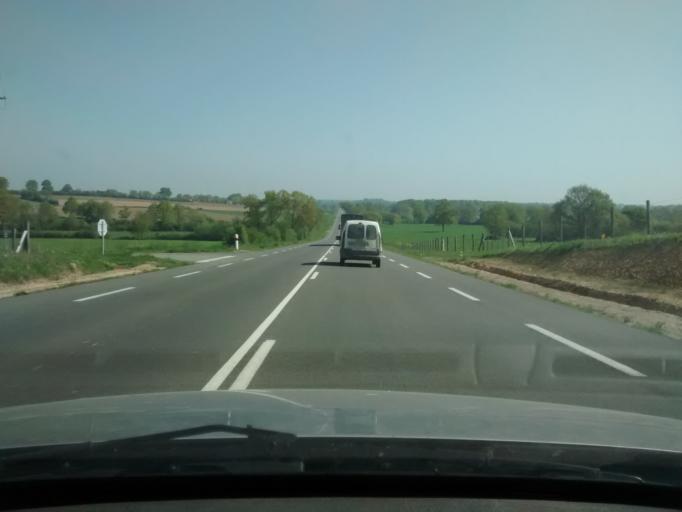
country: FR
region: Pays de la Loire
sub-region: Departement de la Mayenne
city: Soulge-sur-Ouette
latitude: 48.0745
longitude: -0.5519
